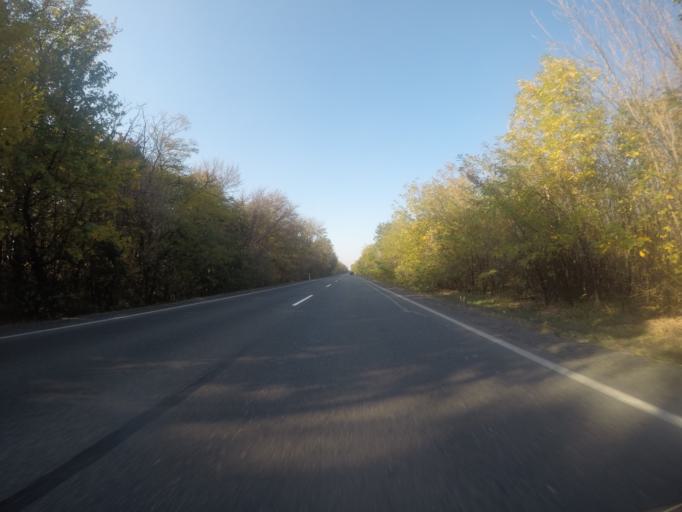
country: HU
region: Fejer
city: Dunaujvaros
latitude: 46.9323
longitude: 18.9263
